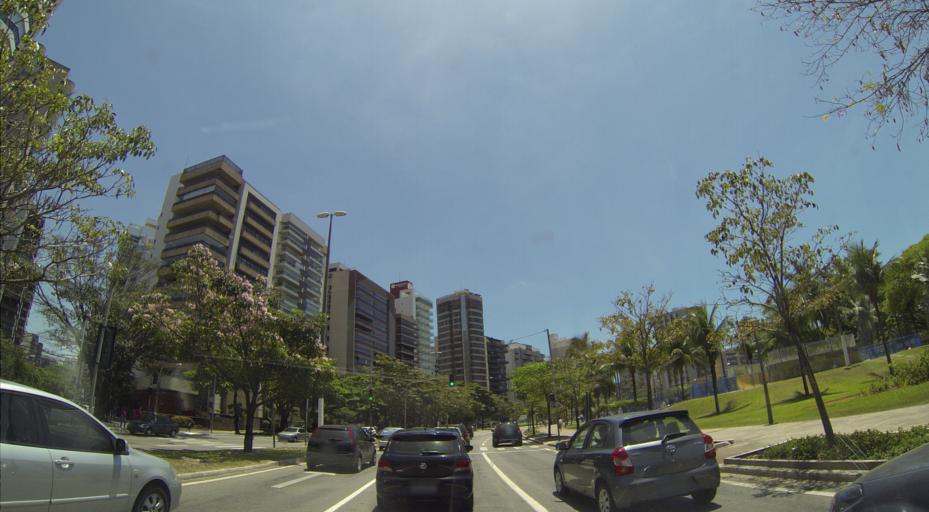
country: BR
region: Espirito Santo
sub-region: Vila Velha
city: Vila Velha
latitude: -20.3000
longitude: -40.2922
